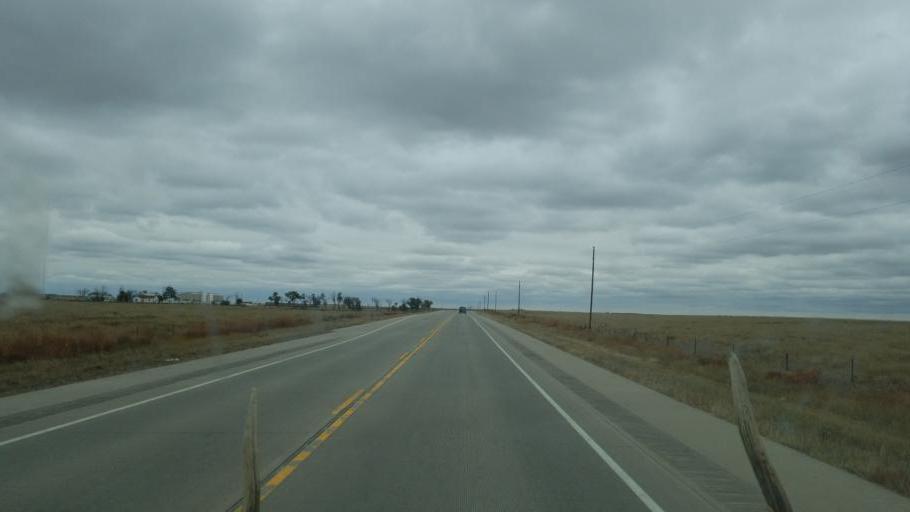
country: US
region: Colorado
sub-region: Kiowa County
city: Eads
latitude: 38.6544
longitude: -102.7860
